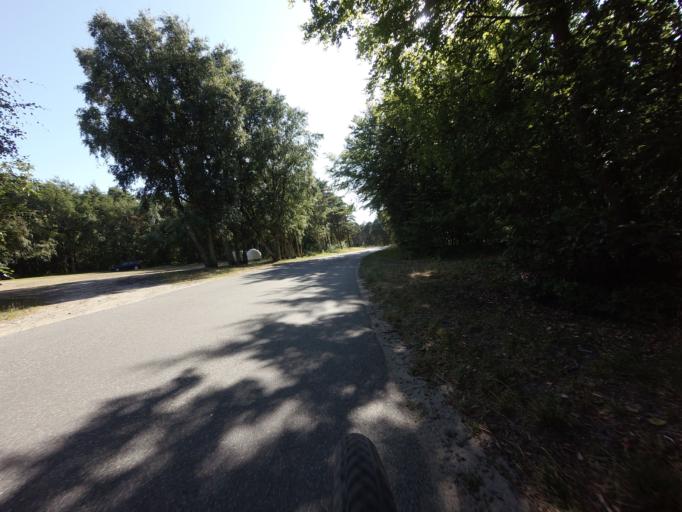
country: DK
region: North Denmark
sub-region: Laeso Kommune
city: Byrum
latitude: 57.2864
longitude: 10.9193
